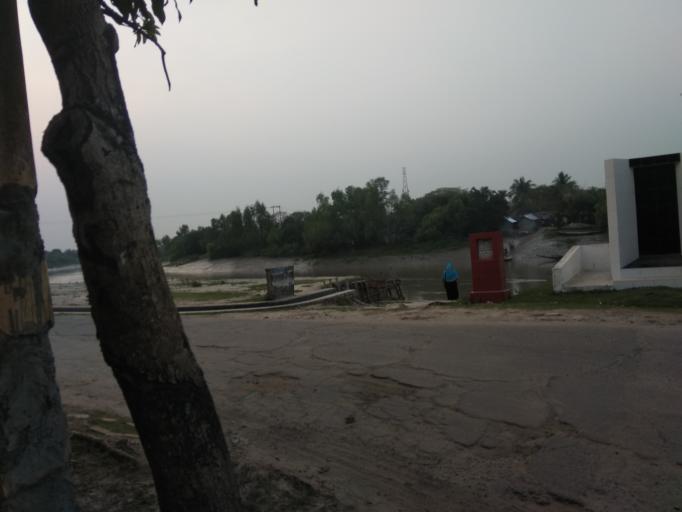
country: IN
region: West Bengal
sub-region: North 24 Parganas
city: Taki
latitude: 22.4564
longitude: 89.0307
